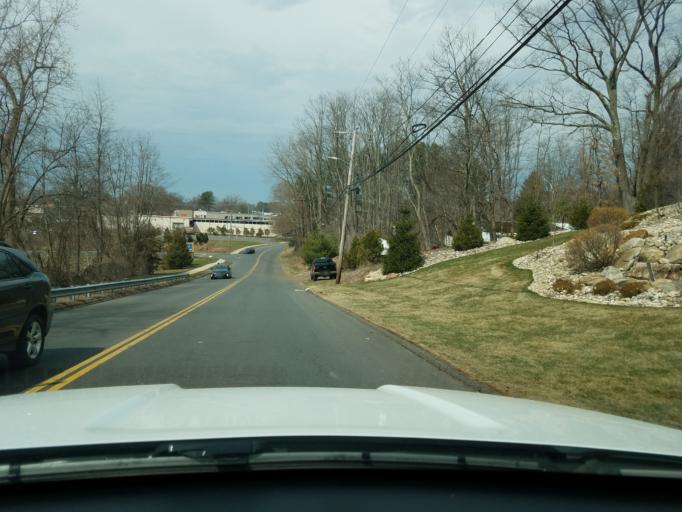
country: US
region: Connecticut
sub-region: Hartford County
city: Newington
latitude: 41.6788
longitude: -72.7096
